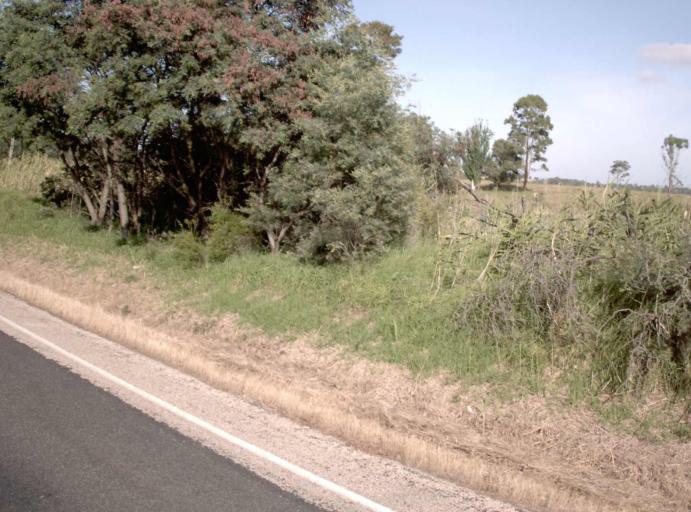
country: AU
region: Victoria
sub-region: East Gippsland
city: Lakes Entrance
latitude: -37.8433
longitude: 147.8545
